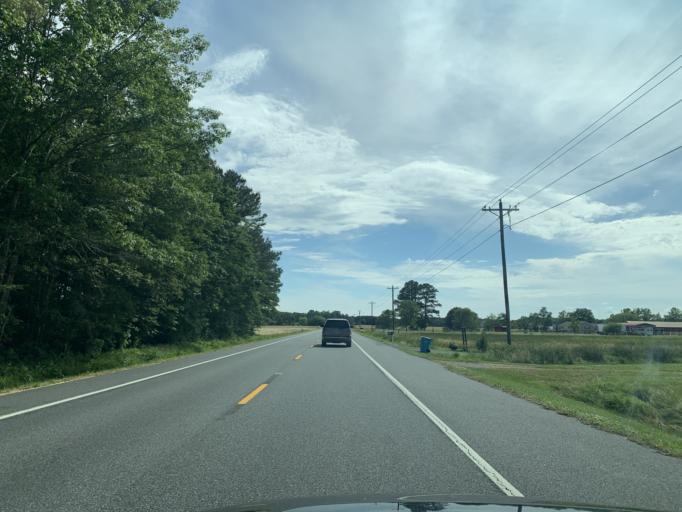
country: US
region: Maryland
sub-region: Worcester County
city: Berlin
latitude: 38.3094
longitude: -75.3129
